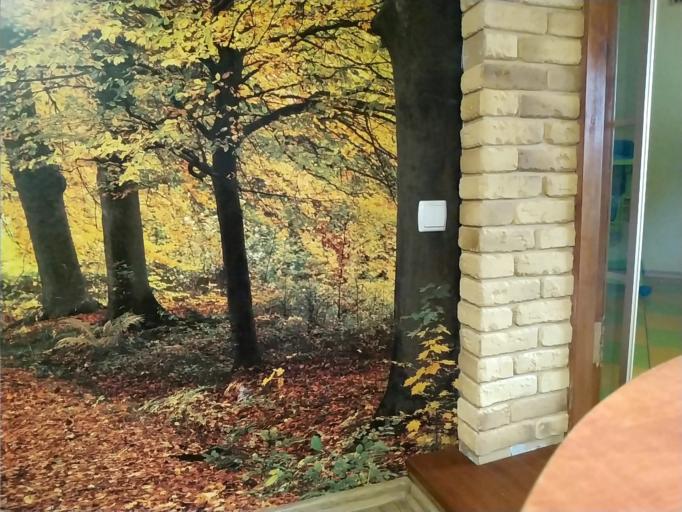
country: RU
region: Smolensk
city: Dorogobuzh
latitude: 54.8964
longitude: 33.3087
